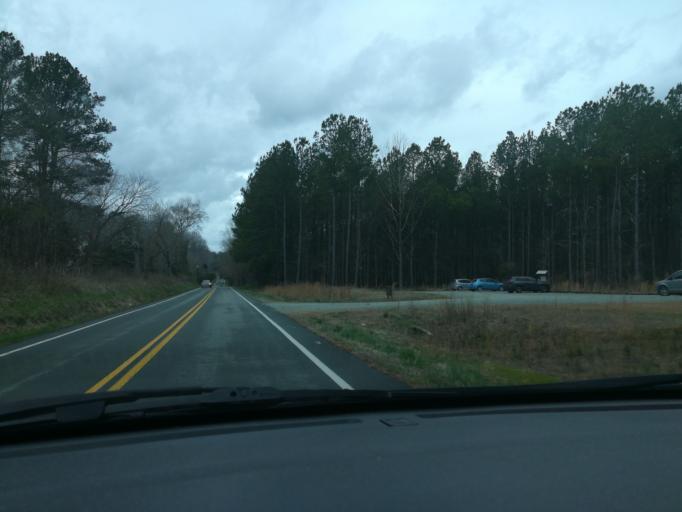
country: US
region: North Carolina
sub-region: Orange County
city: Hillsborough
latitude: 36.0336
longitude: -79.0414
